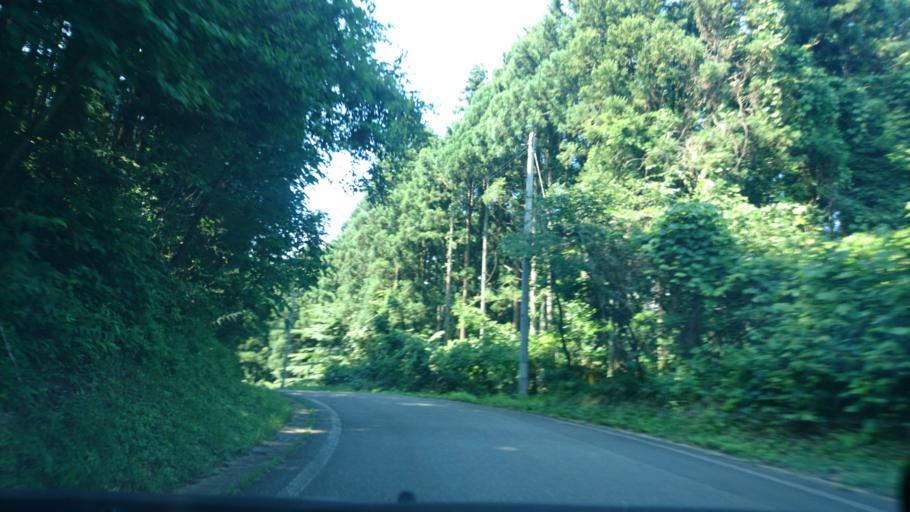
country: JP
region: Iwate
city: Ichinoseki
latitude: 38.9707
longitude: 141.1951
